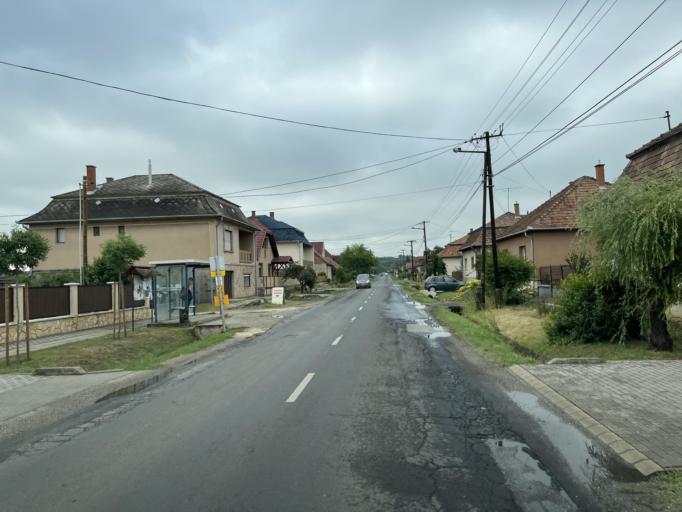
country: HU
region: Pest
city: Hevizgyoerk
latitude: 47.6244
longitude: 19.5307
